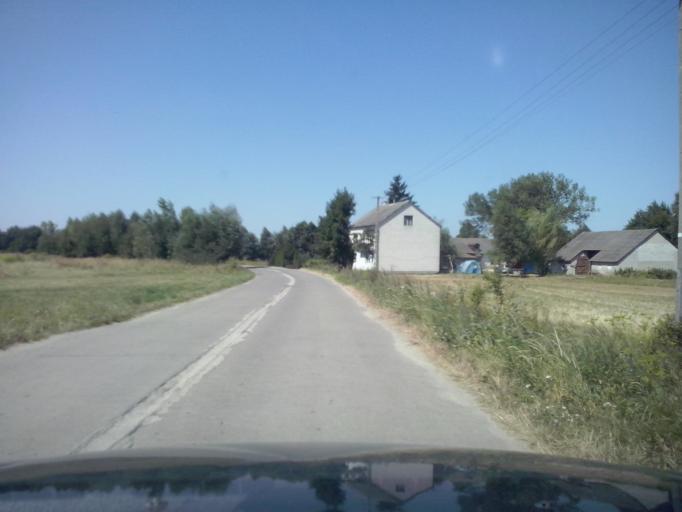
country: PL
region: Swietokrzyskie
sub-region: Powiat buski
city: Gnojno
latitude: 50.5942
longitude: 20.8169
